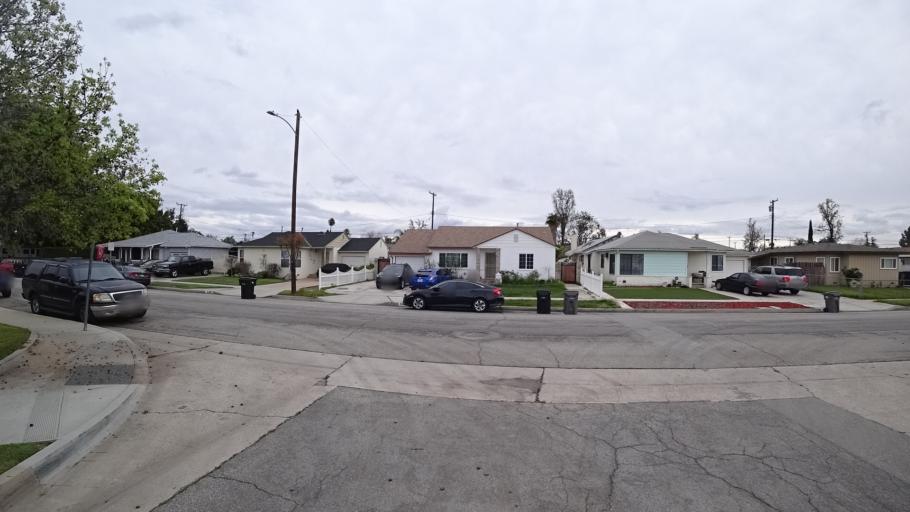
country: US
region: California
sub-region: Los Angeles County
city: Baldwin Park
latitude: 34.0814
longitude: -117.9478
